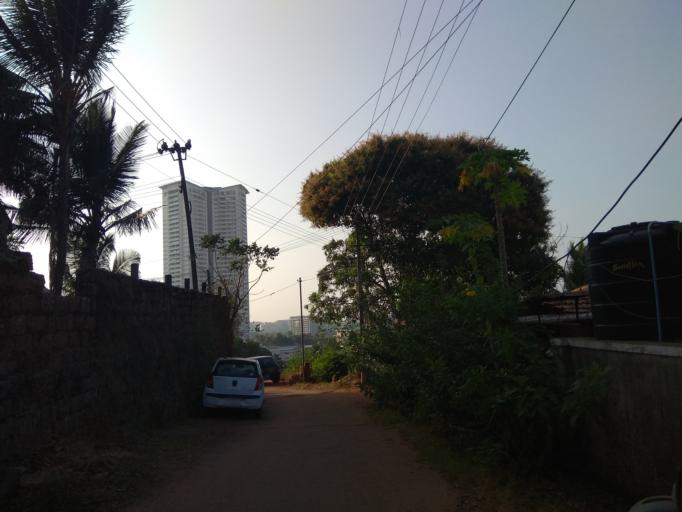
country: IN
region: Karnataka
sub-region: Dakshina Kannada
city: Mangalore
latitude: 12.8926
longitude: 74.8549
